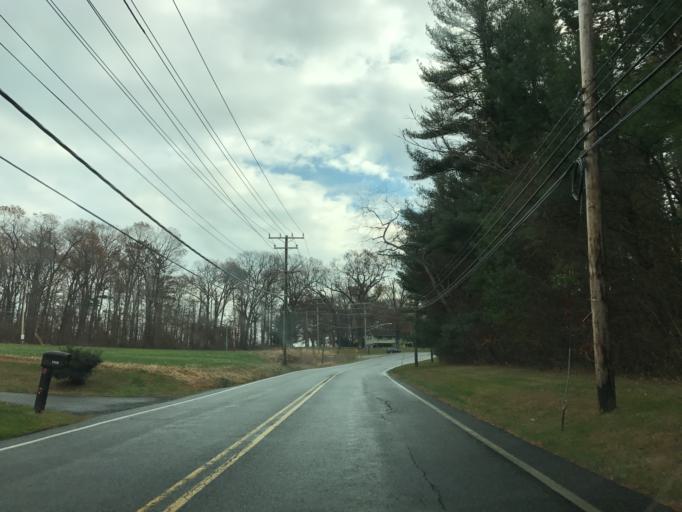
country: US
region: Maryland
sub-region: Harford County
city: Jarrettsville
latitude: 39.6051
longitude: -76.4432
